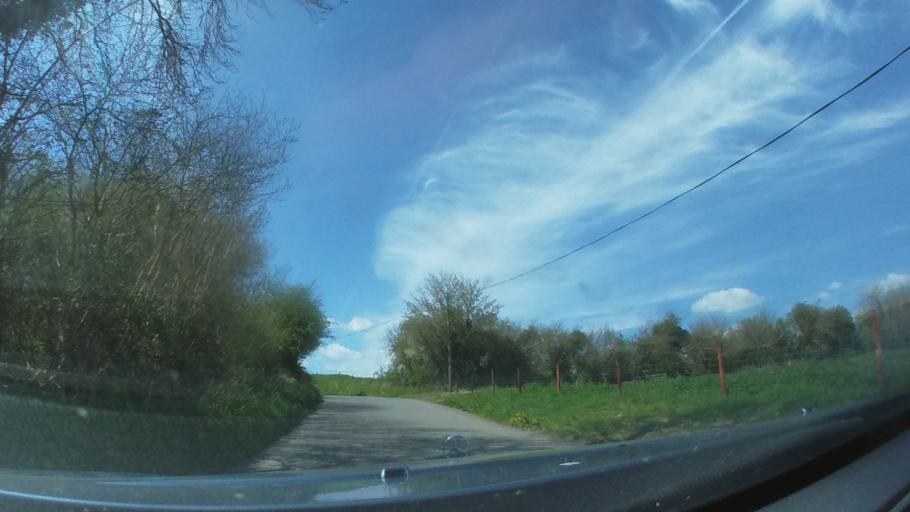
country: IE
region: Leinster
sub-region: Kilkenny
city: Callan
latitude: 52.6257
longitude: -7.4506
